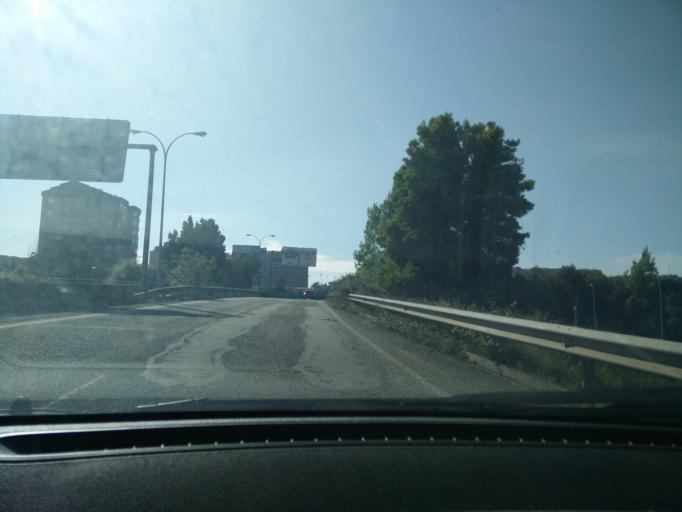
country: ES
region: Galicia
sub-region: Provincia de Pontevedra
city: Vigo
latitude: 42.2086
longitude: -8.7487
